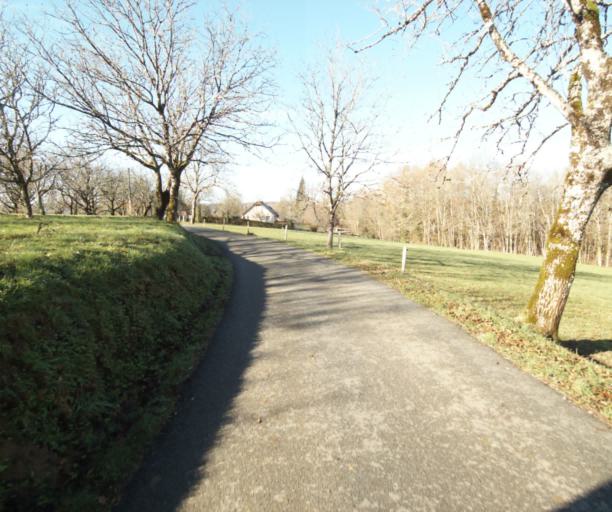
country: FR
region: Limousin
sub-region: Departement de la Correze
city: Sainte-Fortunade
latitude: 45.2301
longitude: 1.7417
